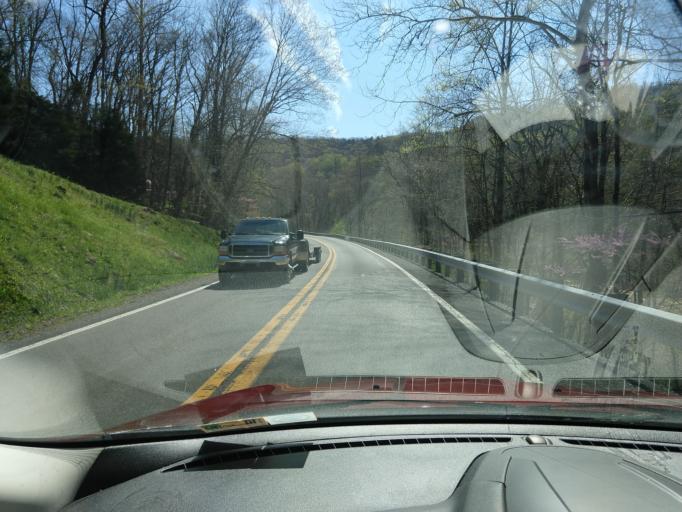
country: US
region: West Virginia
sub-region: Greenbrier County
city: Alderson
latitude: 37.7175
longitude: -80.6210
